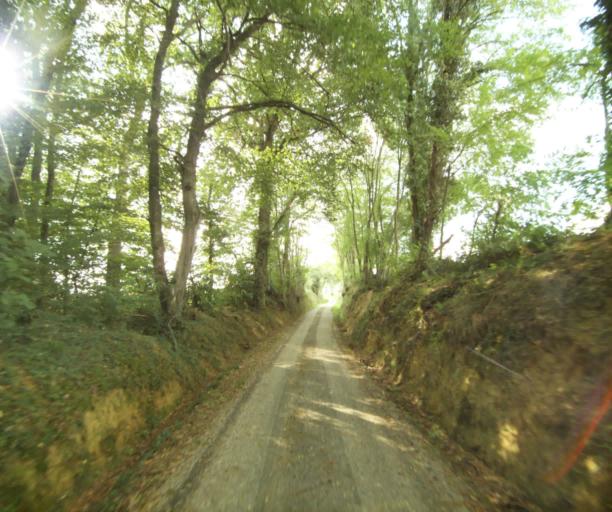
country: FR
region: Midi-Pyrenees
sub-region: Departement du Gers
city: Cazaubon
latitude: 43.8961
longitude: -0.0960
